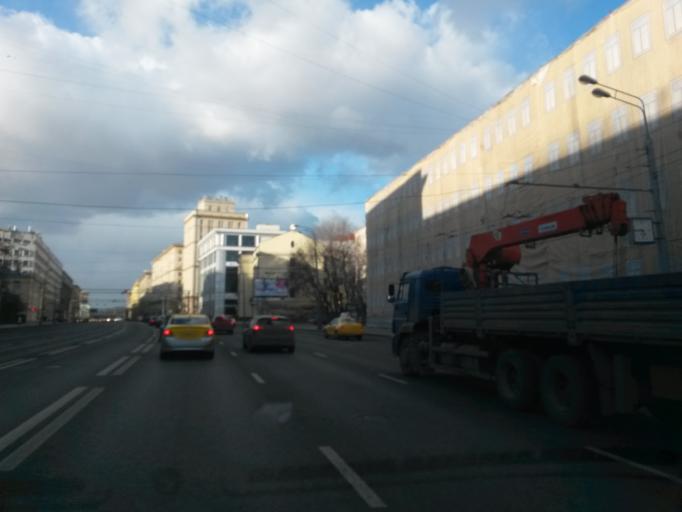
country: RU
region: Moscow
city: Mar'ina Roshcha
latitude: 55.7844
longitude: 37.6350
